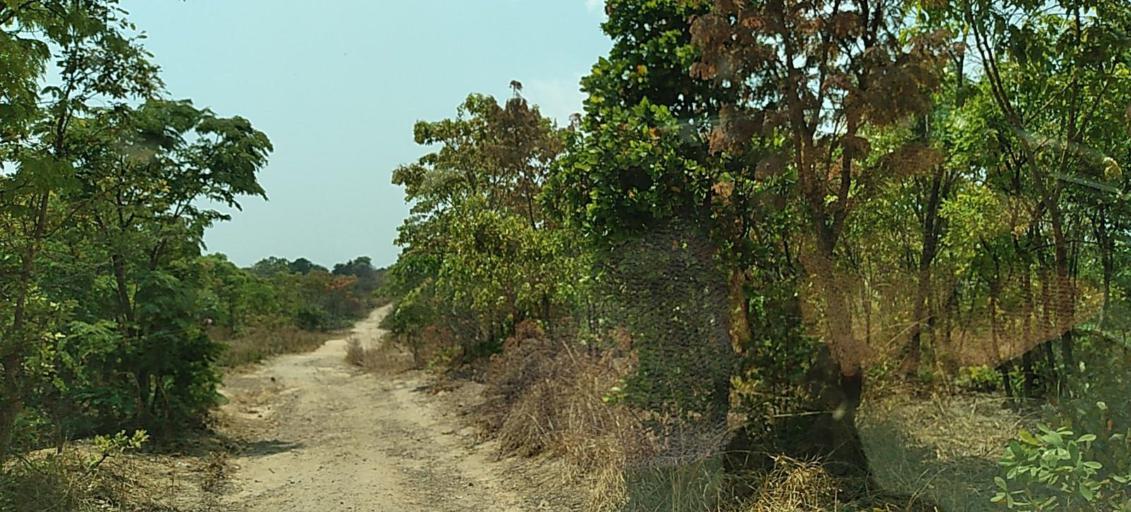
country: ZM
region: Copperbelt
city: Kalulushi
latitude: -12.9526
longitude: 28.1380
